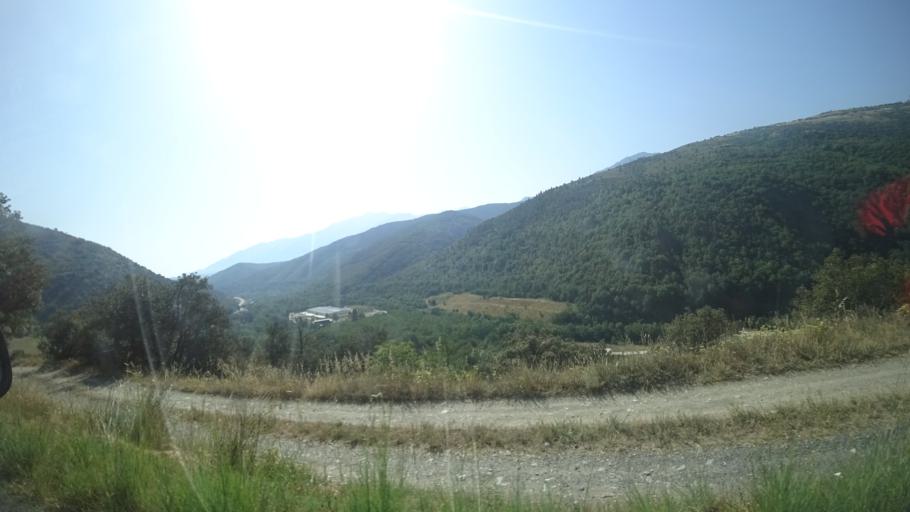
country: FR
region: Languedoc-Roussillon
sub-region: Departement des Pyrenees-Orientales
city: Vernet-les-Bains
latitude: 42.5609
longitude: 2.2850
